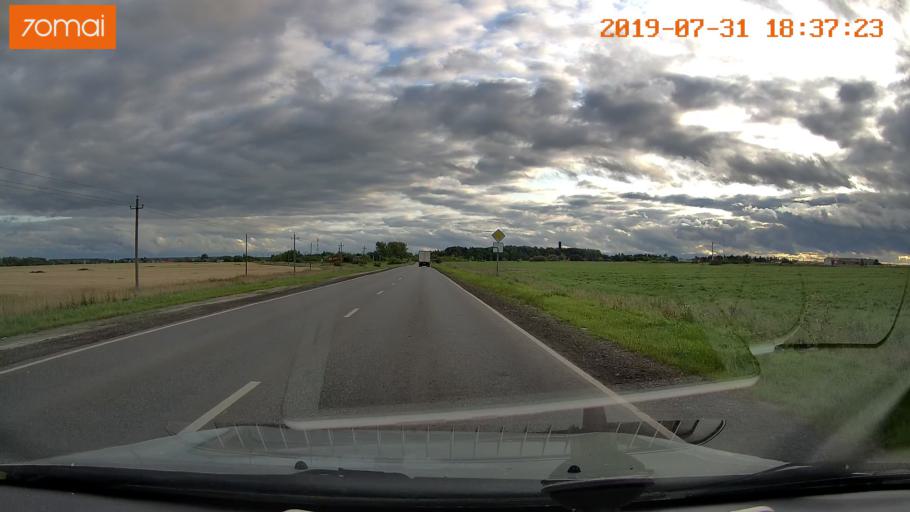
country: RU
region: Moskovskaya
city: Voskresensk
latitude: 55.2794
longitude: 38.6617
